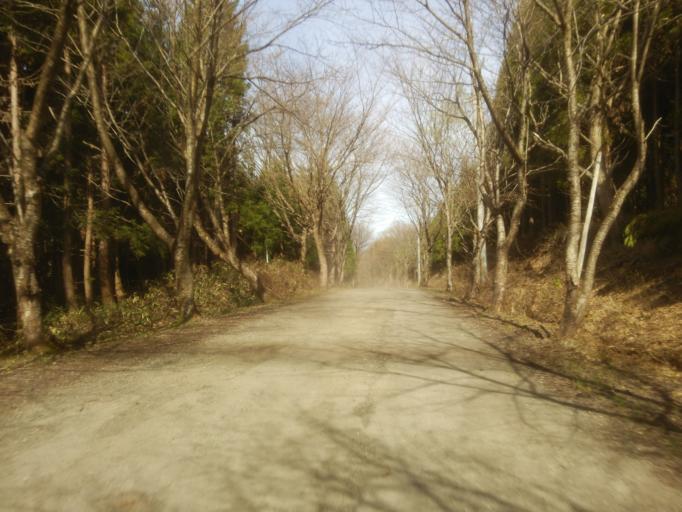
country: JP
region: Fukushima
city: Inawashiro
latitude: 37.5272
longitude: 140.0360
